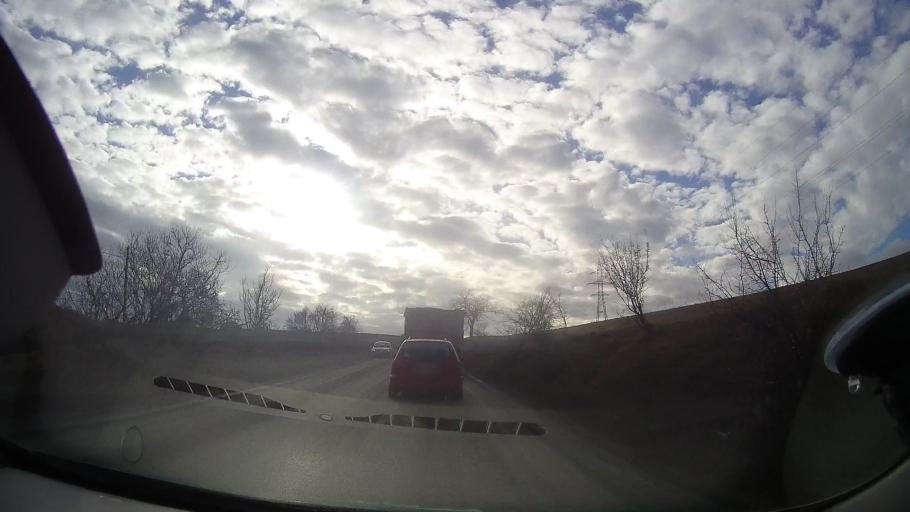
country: RO
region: Cluj
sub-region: Comuna Savadisla
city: Savadisla
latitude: 46.6545
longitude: 23.4527
